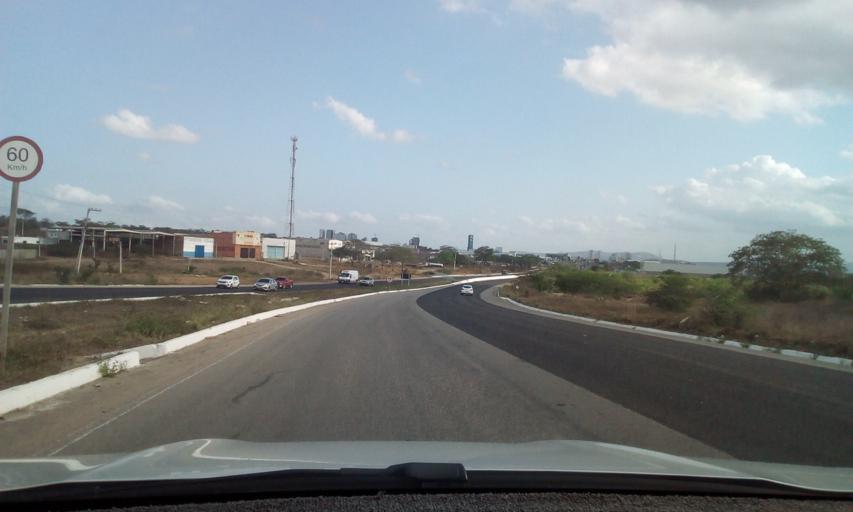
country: BR
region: Pernambuco
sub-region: Caruaru
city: Caruaru
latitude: -8.2362
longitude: -35.9760
